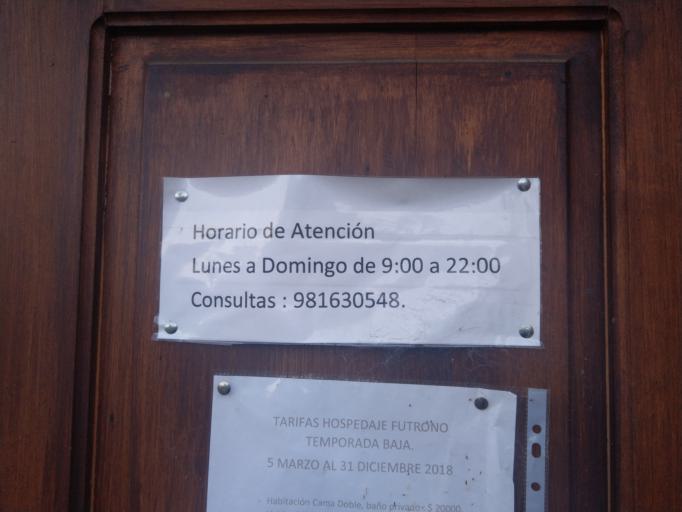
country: CL
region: Araucania
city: Panguipulli
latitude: -40.1340
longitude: -72.3882
